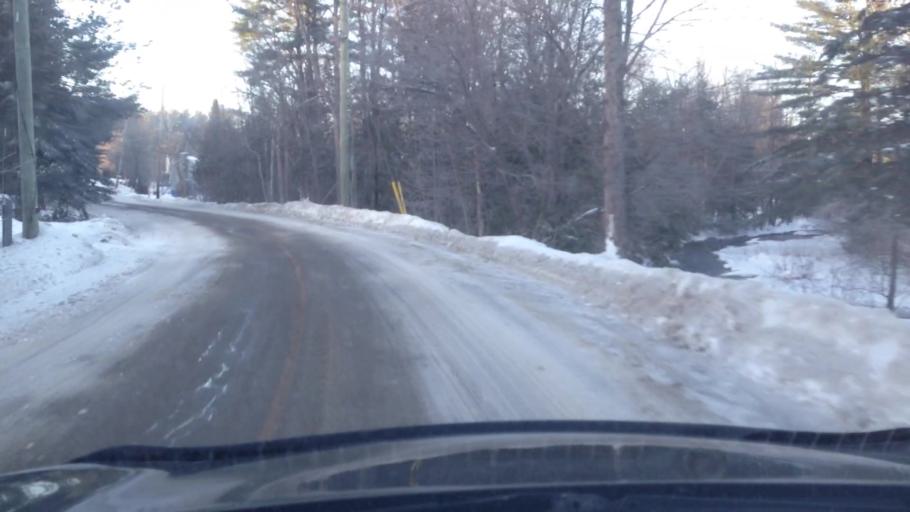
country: CA
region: Quebec
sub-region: Lanaudiere
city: Sainte-Julienne
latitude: 45.9485
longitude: -73.7475
